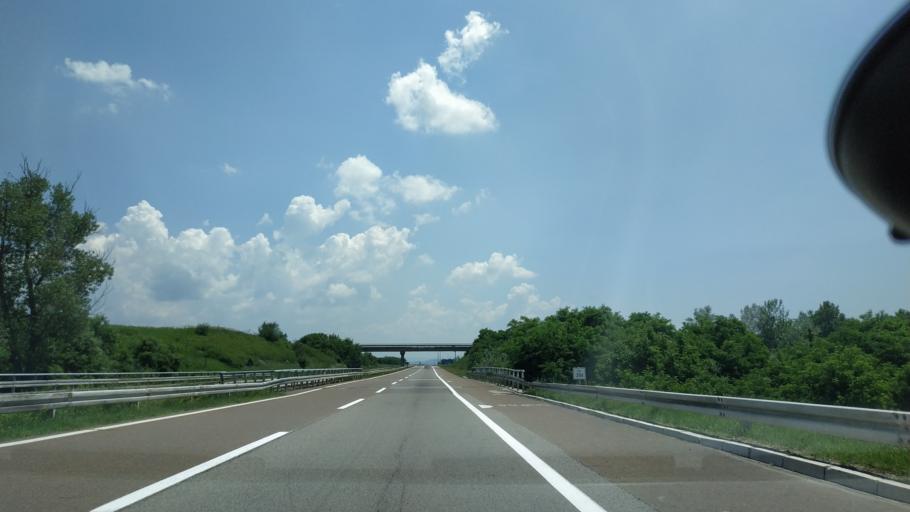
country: RS
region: Central Serbia
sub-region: Nisavski Okrug
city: Razanj
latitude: 43.6202
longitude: 21.5864
